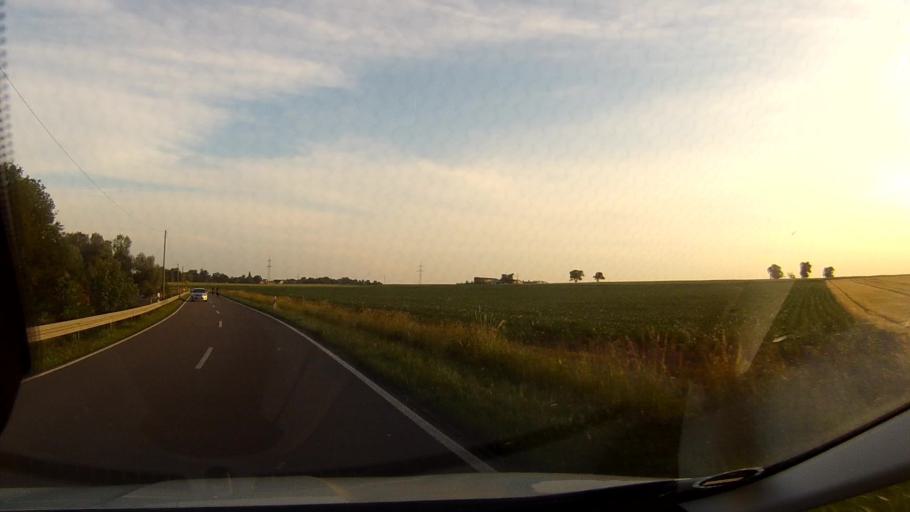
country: DE
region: Bavaria
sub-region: Swabia
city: Senden
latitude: 48.3174
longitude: 10.0203
